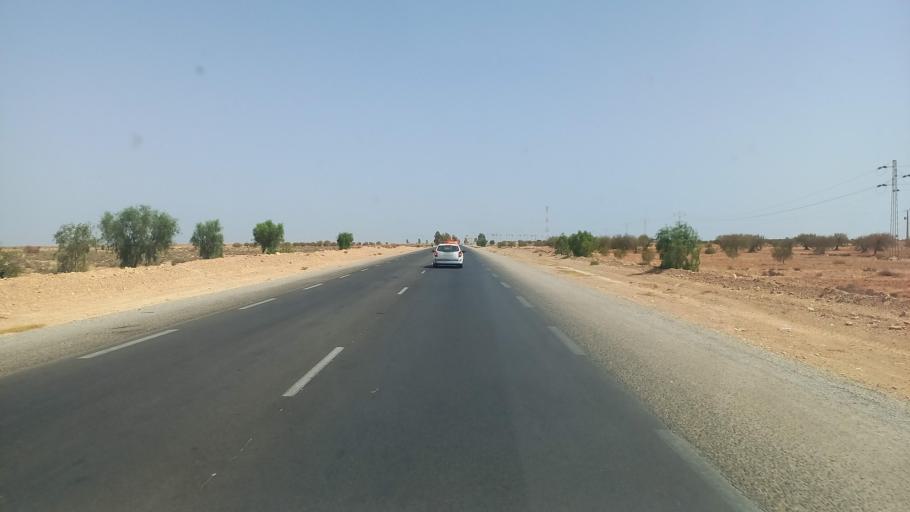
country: TN
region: Madanin
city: Medenine
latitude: 33.3800
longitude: 10.6984
